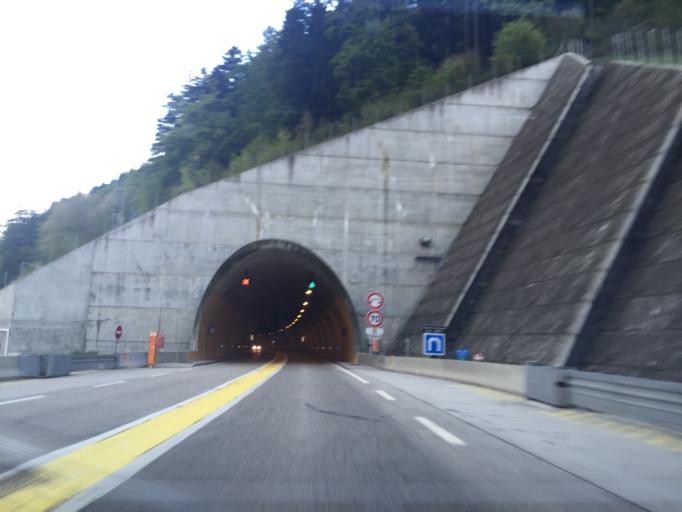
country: FR
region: Rhone-Alpes
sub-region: Departement de l'Isere
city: La Motte-Saint-Martin
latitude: 44.9338
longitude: 5.6420
